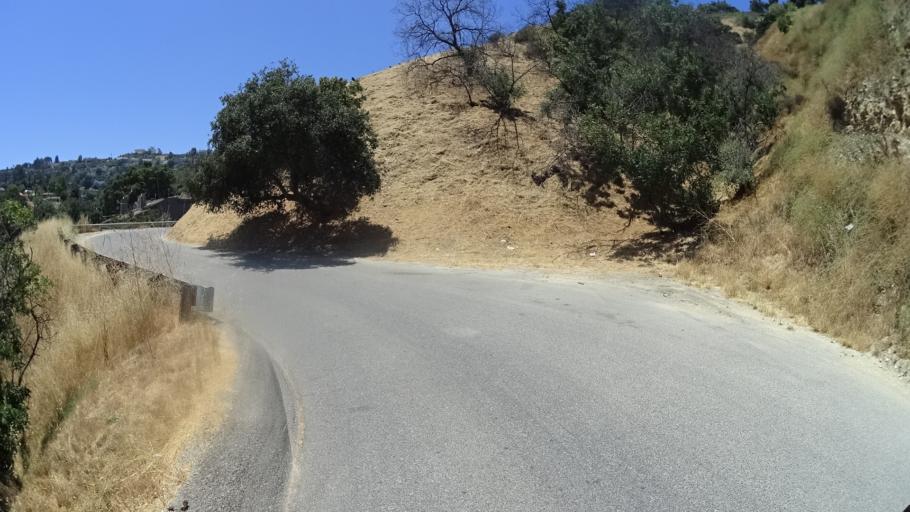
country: US
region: California
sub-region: Los Angeles County
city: Sherman Oaks
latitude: 34.1377
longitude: -118.4459
